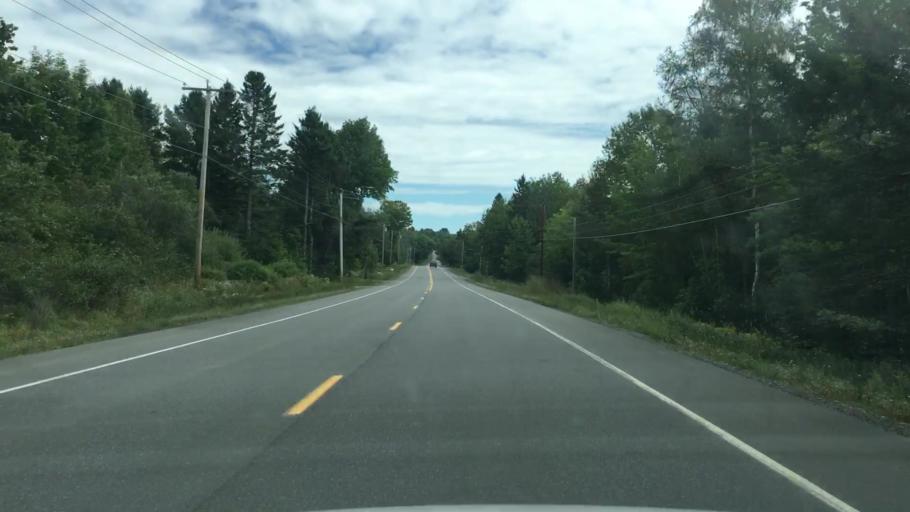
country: US
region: Maine
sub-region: Piscataquis County
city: Milo
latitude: 45.2417
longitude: -69.0309
